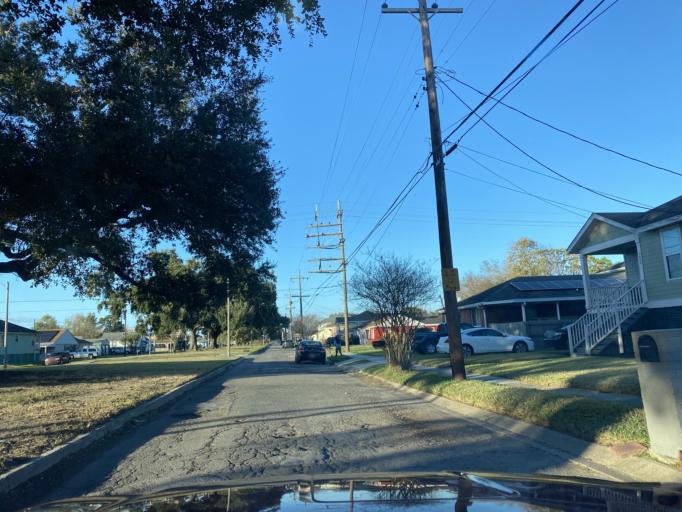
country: US
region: Louisiana
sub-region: Orleans Parish
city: New Orleans
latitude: 30.0144
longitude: -90.0556
